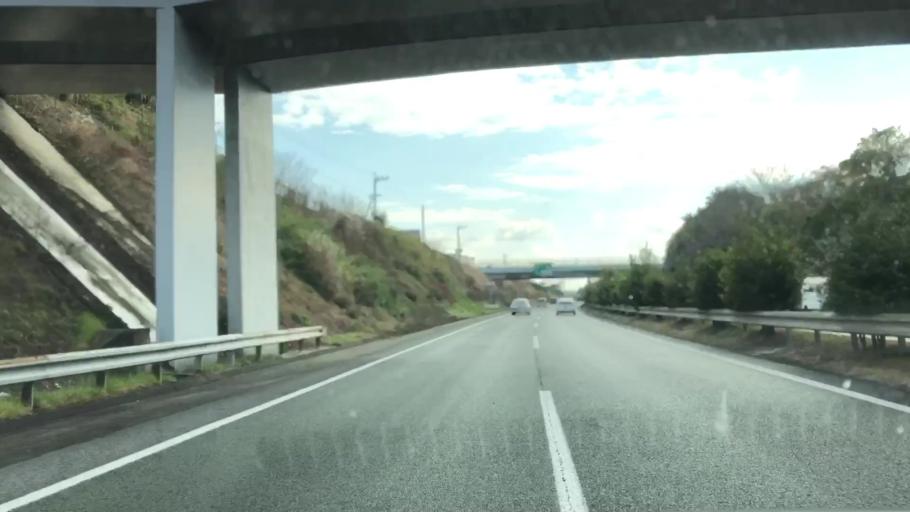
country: JP
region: Fukuoka
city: Setakamachi-takayanagi
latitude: 33.1333
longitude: 130.5169
